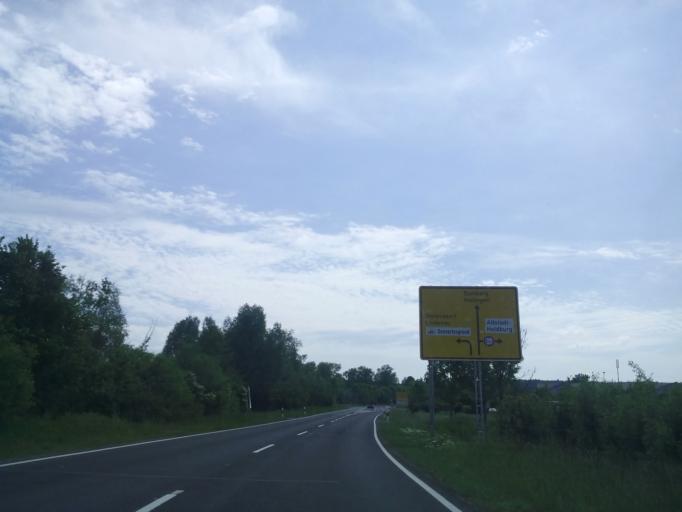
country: DE
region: Thuringia
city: Hellingen
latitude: 50.2767
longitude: 10.7303
